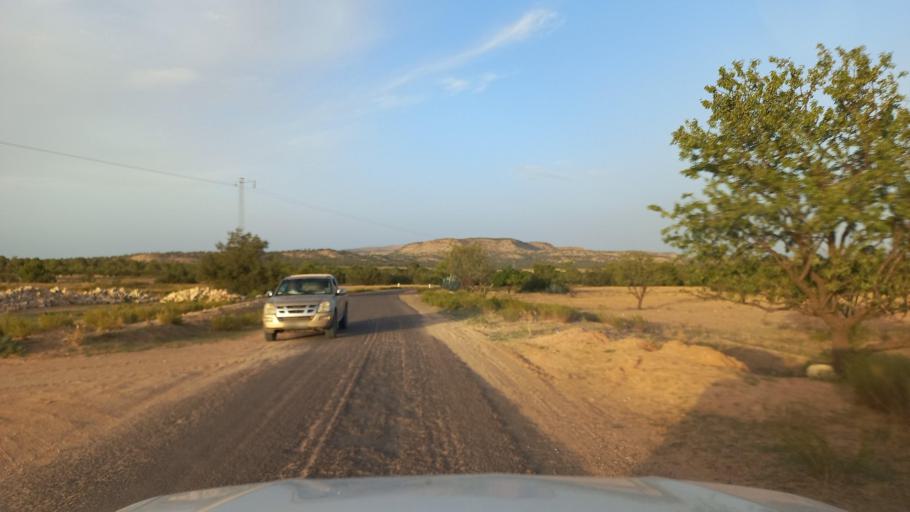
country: TN
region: Al Qasrayn
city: Sbiba
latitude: 35.4089
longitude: 8.9150
